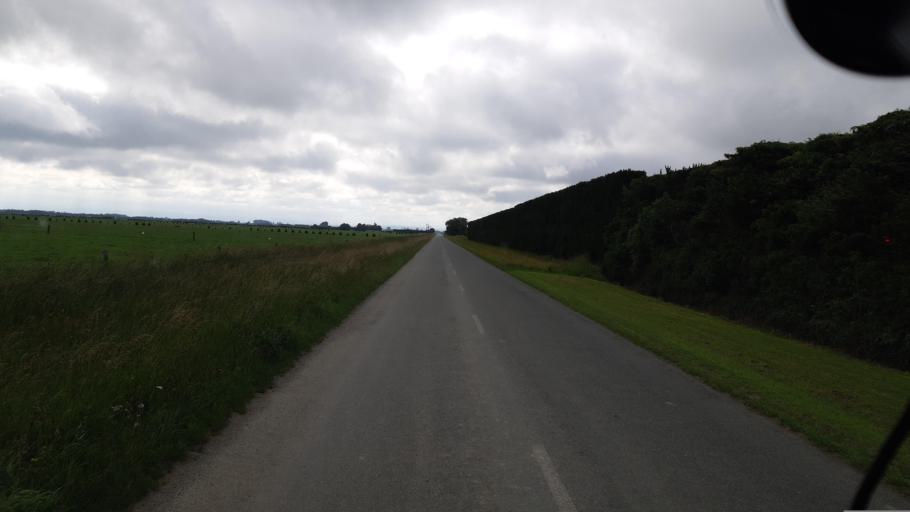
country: NZ
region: Canterbury
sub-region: Timaru District
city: Timaru
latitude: -44.2435
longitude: 171.3611
